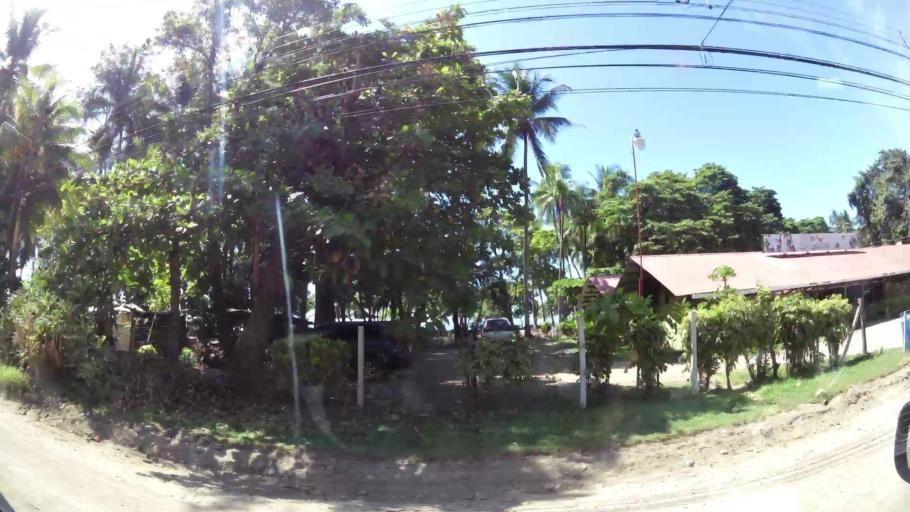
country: CR
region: San Jose
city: San Isidro
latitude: 9.2520
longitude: -83.8641
